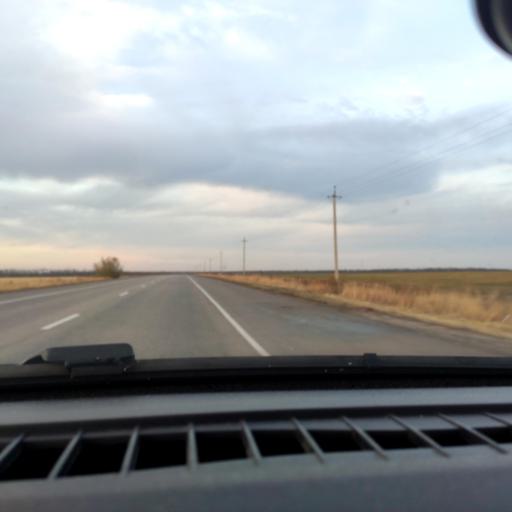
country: RU
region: Voronezj
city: Strelitsa
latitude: 51.5618
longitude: 38.9733
